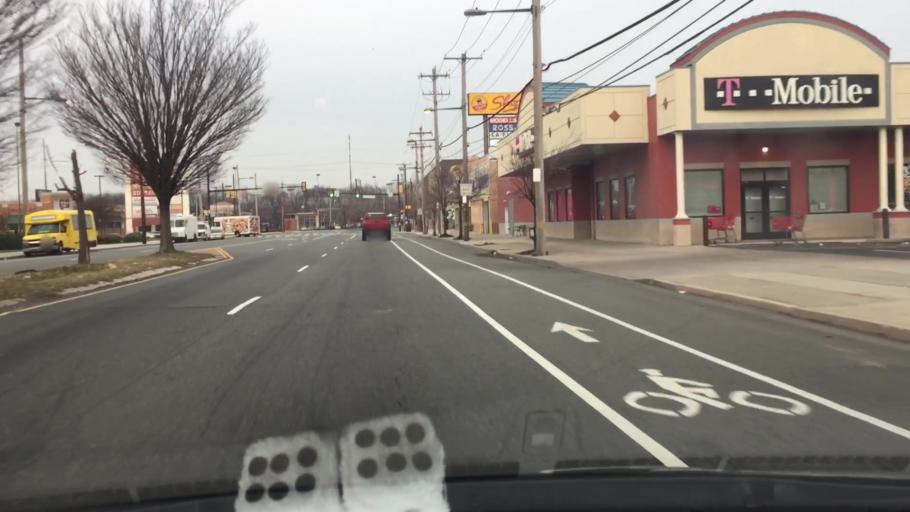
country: US
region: Pennsylvania
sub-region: Philadelphia County
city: Philadelphia
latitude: 39.9186
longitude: -75.1846
